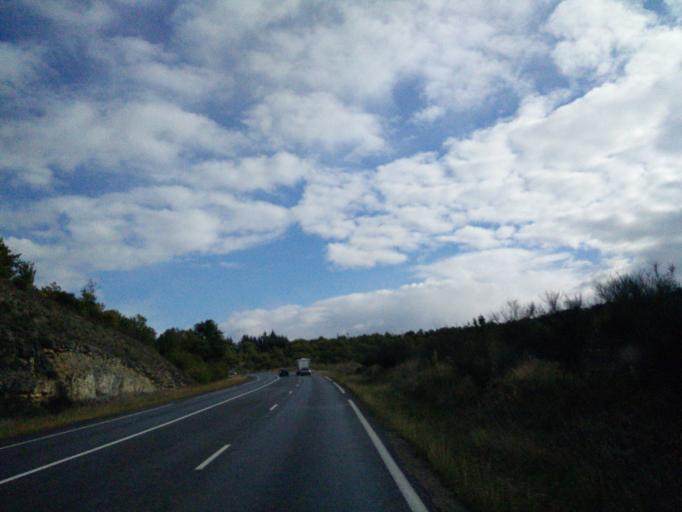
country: FR
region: Midi-Pyrenees
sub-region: Departement du Lot
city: Cahors
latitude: 44.4498
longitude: 1.4141
